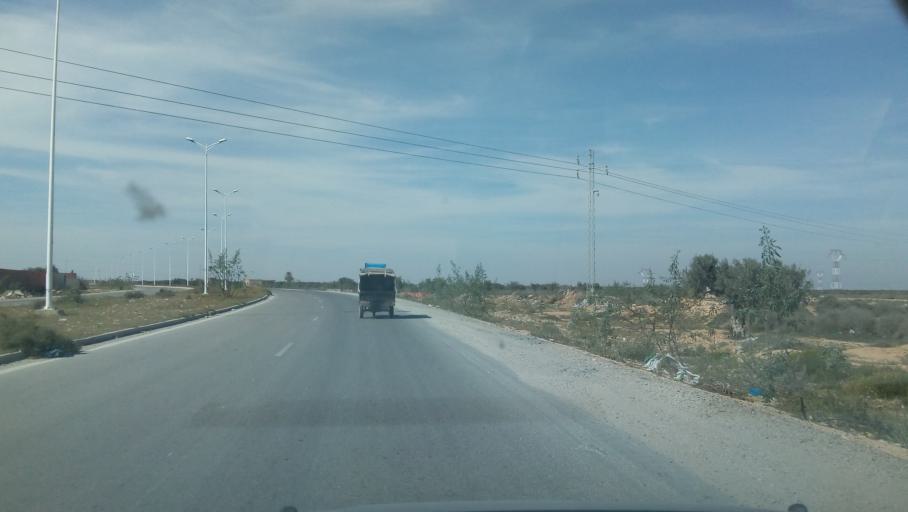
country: TN
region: Safaqis
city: Al Qarmadah
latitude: 34.8370
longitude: 10.8480
